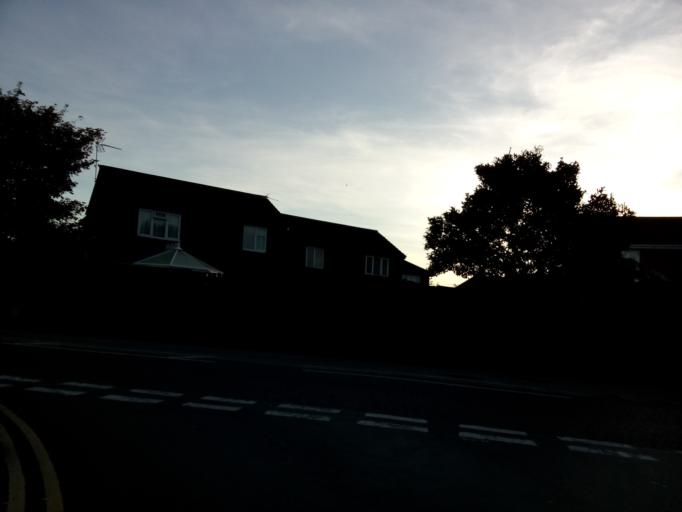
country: GB
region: England
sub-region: Suffolk
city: Bramford
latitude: 52.0426
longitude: 1.1076
